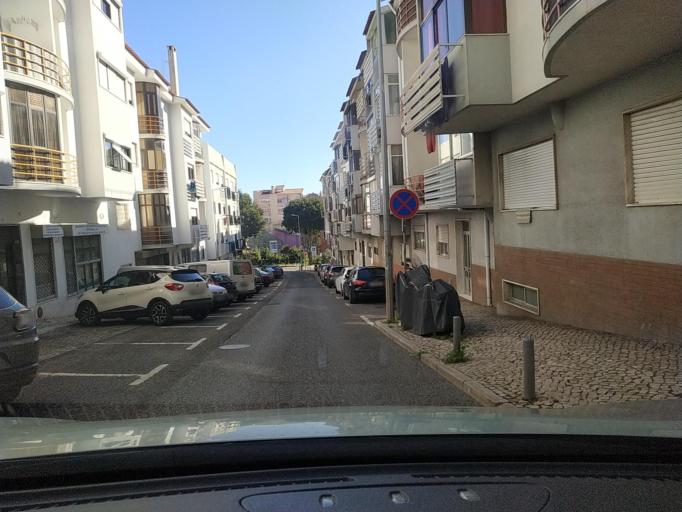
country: PT
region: Lisbon
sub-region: Amadora
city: Amadora
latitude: 38.7674
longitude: -9.2235
